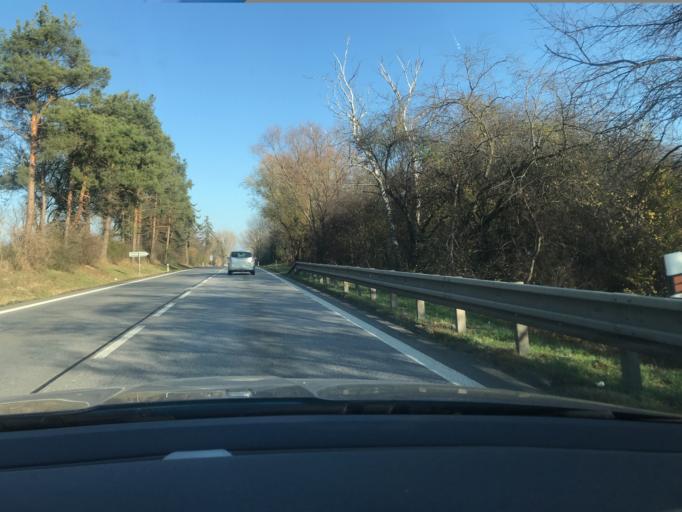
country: CZ
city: Predmerice nad Labem
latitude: 50.2767
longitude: 15.8155
